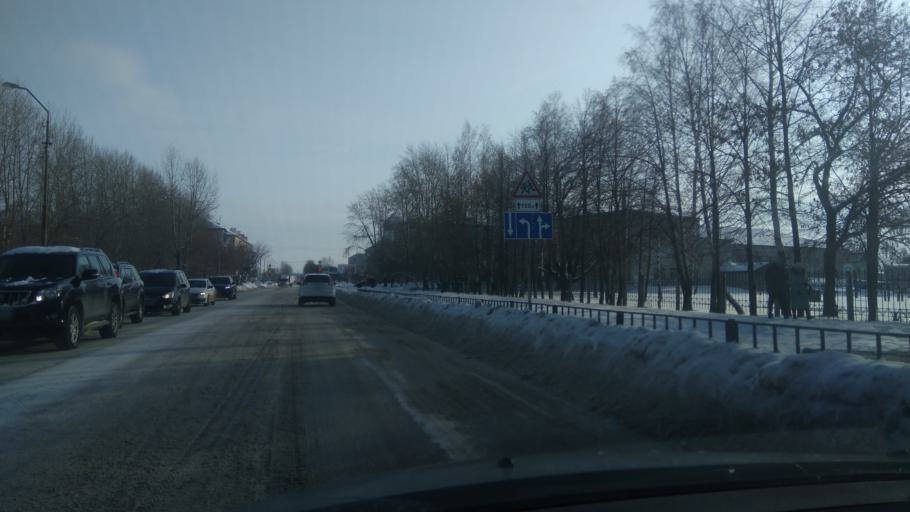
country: RU
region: Sverdlovsk
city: Sukhoy Log
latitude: 56.8998
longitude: 62.0290
